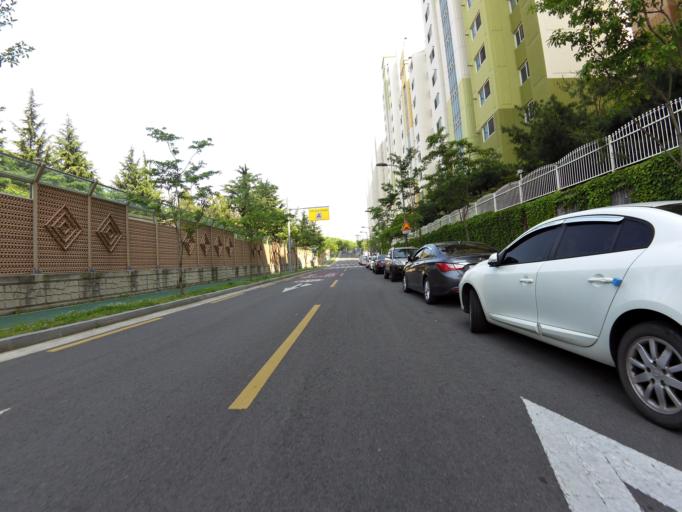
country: KR
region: Daegu
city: Daegu
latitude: 35.8745
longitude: 128.6537
